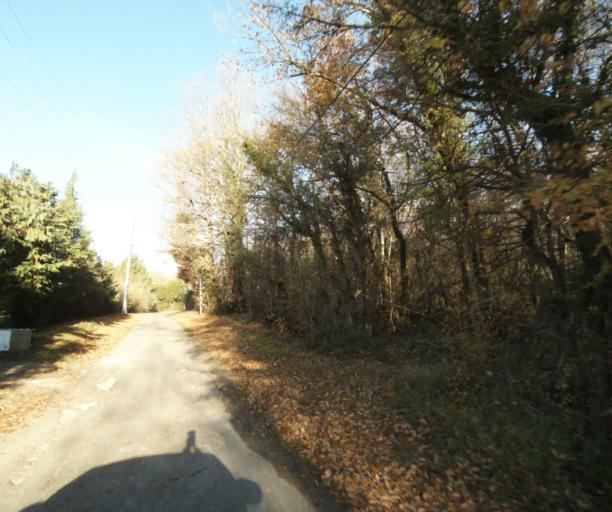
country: FR
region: Poitou-Charentes
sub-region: Departement de la Charente-Maritime
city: Cherac
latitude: 45.7091
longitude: -0.4567
